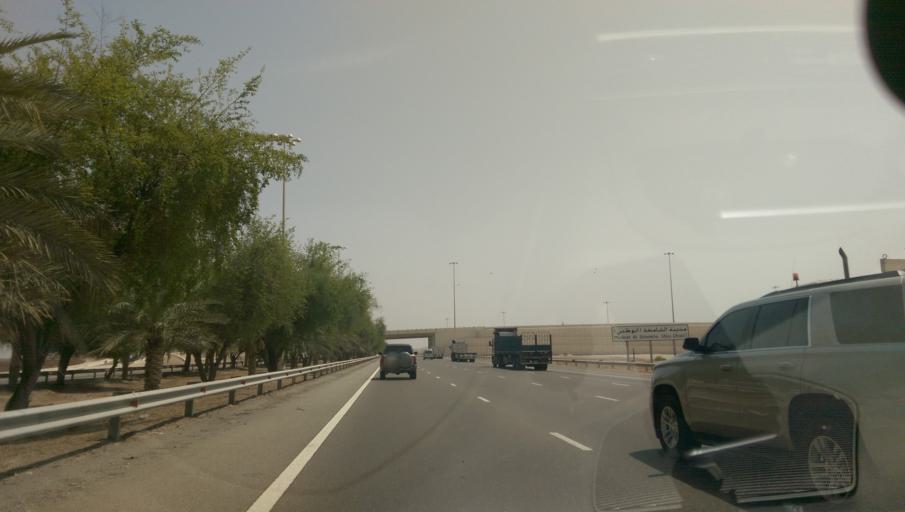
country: AE
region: Abu Dhabi
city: Abu Dhabi
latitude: 24.3667
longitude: 54.6533
